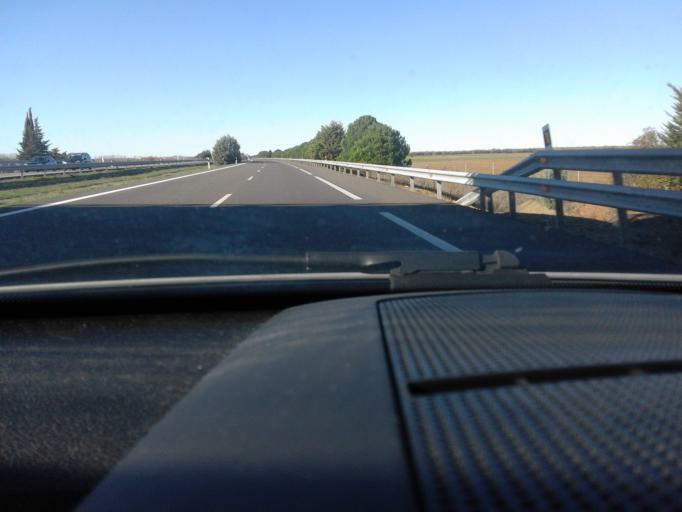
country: ES
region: Castille and Leon
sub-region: Provincia de Leon
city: Calzada del Coto
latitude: 42.3865
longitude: -5.0961
